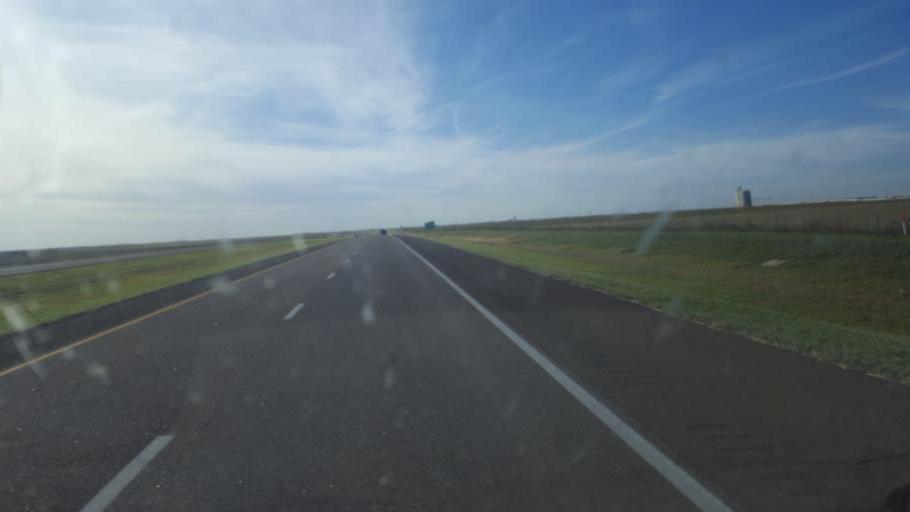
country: US
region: Kansas
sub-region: Trego County
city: WaKeeney
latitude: 39.0033
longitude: -99.8287
